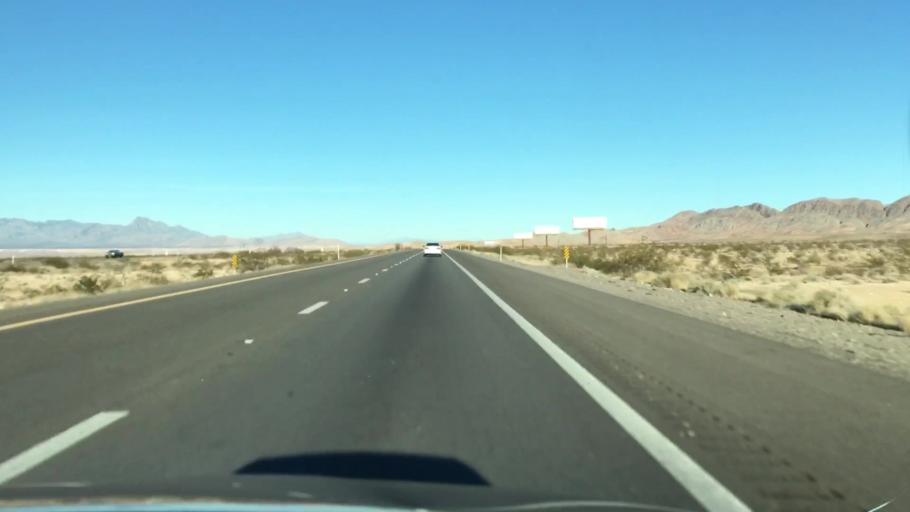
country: US
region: Nevada
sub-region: Clark County
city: Moapa Town
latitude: 36.5715
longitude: -114.6685
